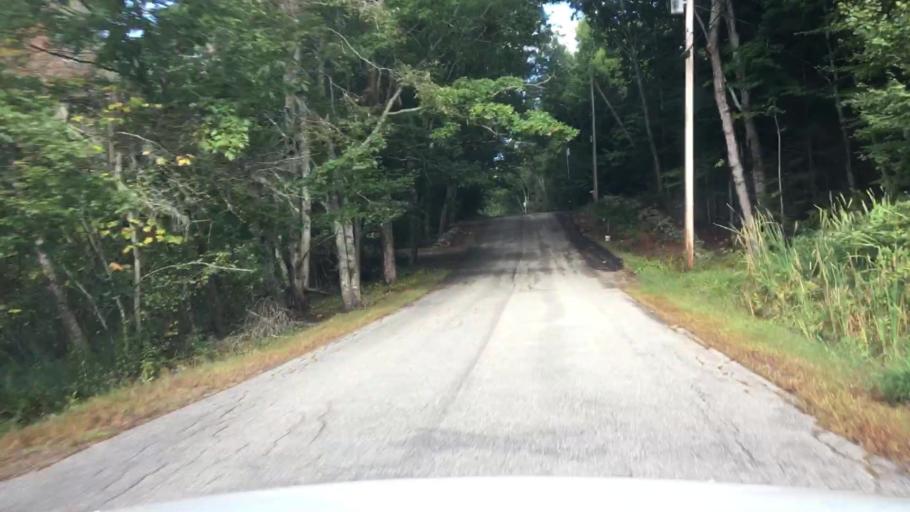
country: US
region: Maine
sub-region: York County
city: York Harbor
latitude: 43.1167
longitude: -70.6748
